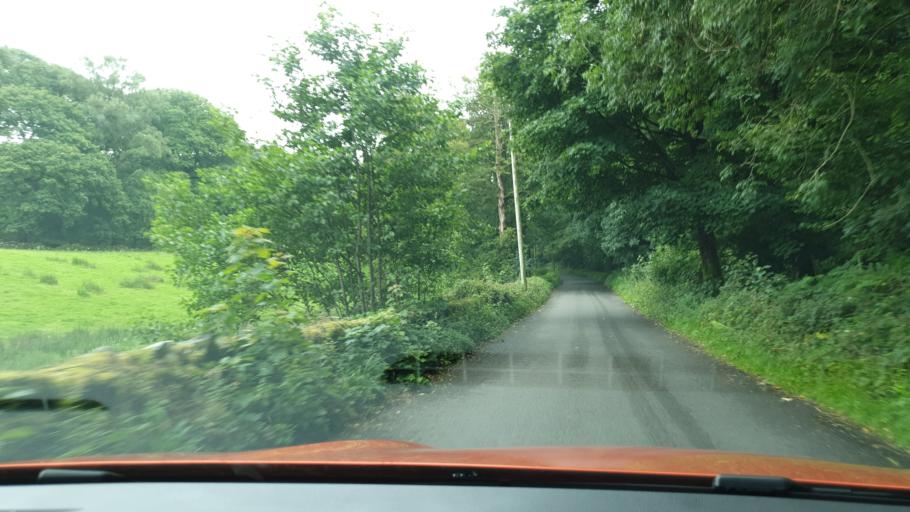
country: GB
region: England
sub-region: Cumbria
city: Grange-over-Sands
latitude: 54.2716
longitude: -2.9864
